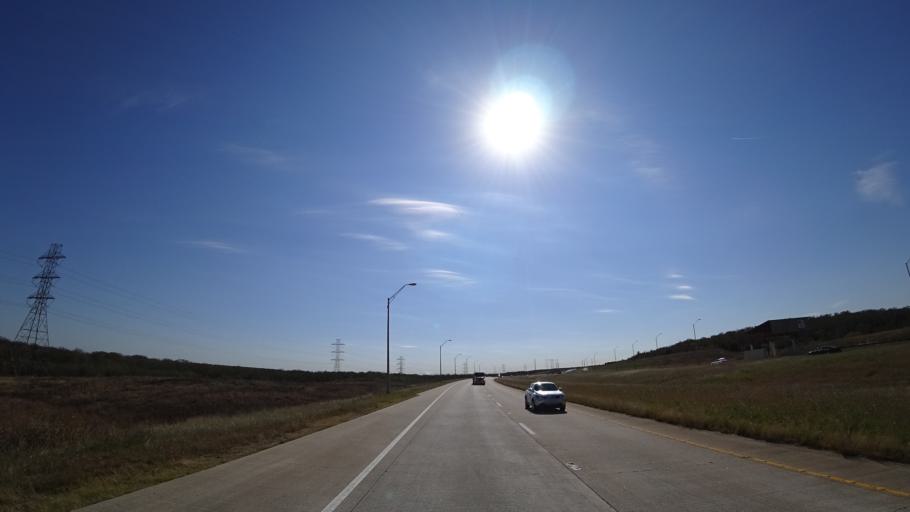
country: US
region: Texas
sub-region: Travis County
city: Manor
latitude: 30.3073
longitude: -97.5693
